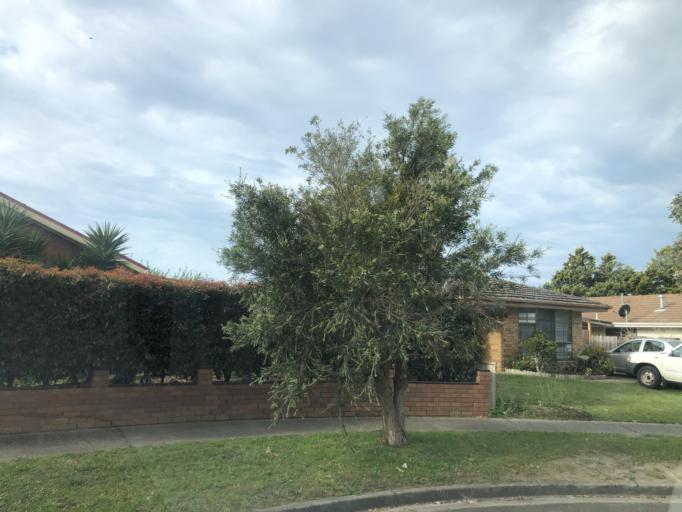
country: AU
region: Victoria
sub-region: Casey
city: Hampton Park
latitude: -38.0250
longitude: 145.2559
